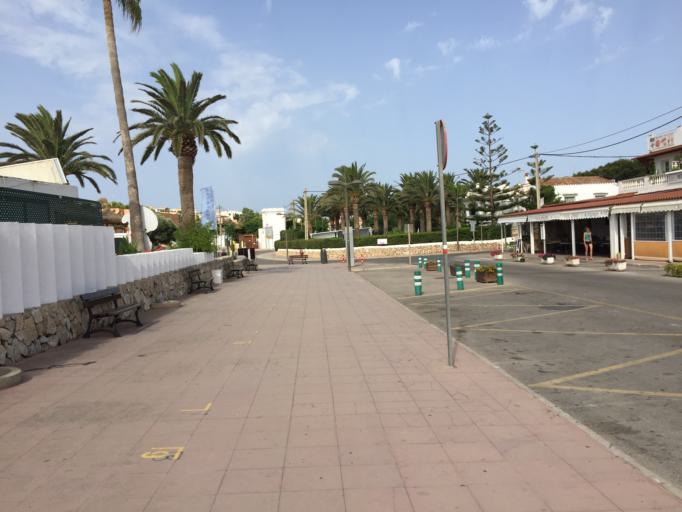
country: ES
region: Balearic Islands
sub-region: Illes Balears
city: Sant Lluis
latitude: 39.8142
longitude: 4.2804
